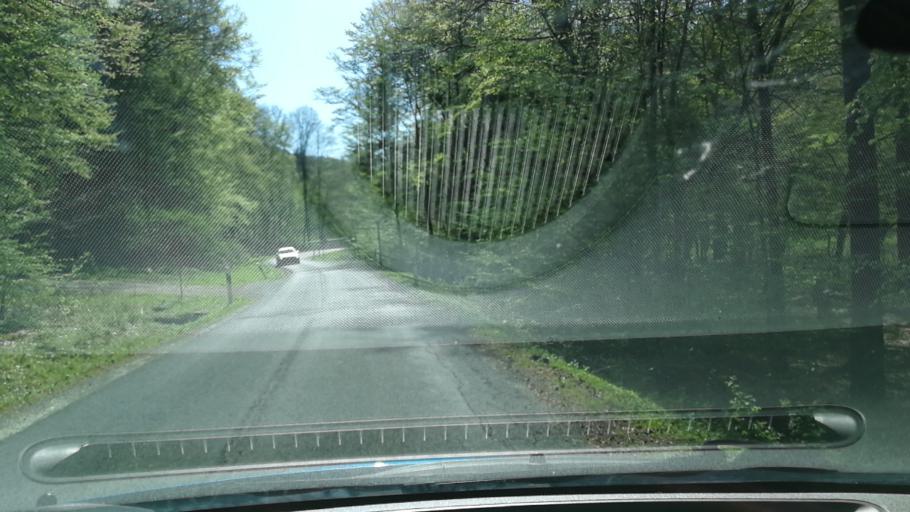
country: DE
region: Lower Saxony
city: Buhren
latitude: 51.5397
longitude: 9.6604
